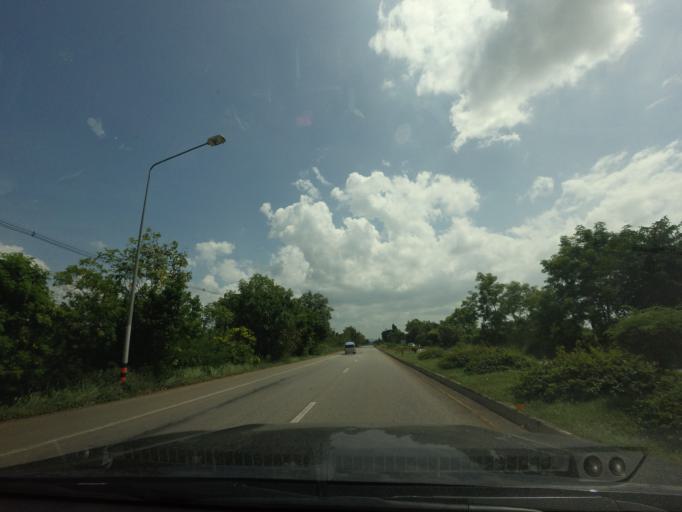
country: TH
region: Phetchabun
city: Phetchabun
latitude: 16.2447
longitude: 101.0736
